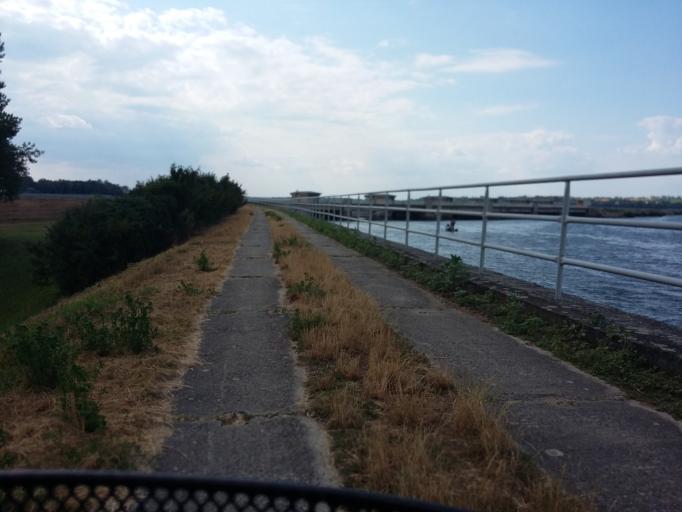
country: CZ
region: South Moravian
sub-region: Okres Breclav
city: Dolni Dunajovice
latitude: 48.8922
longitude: 16.6458
